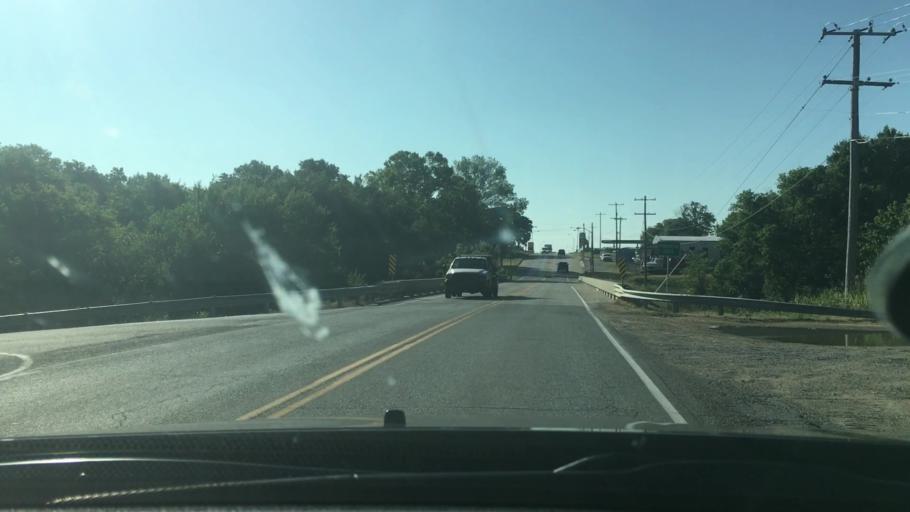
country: US
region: Oklahoma
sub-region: Johnston County
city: Tishomingo
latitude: 34.2396
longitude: -96.6858
